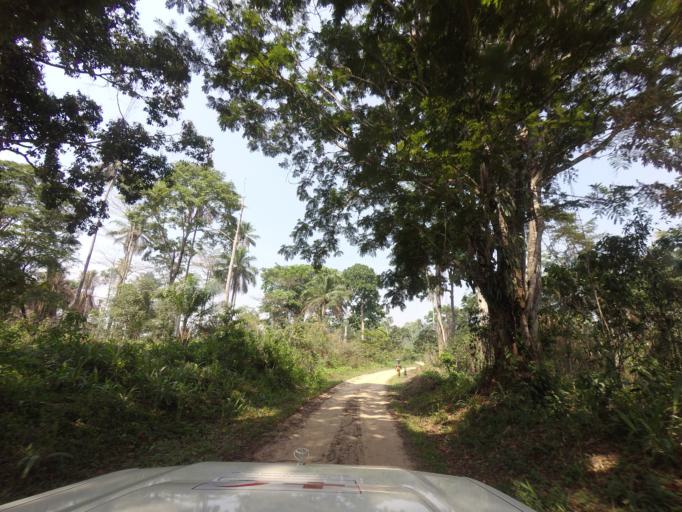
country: LR
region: Lofa
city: Voinjama
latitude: 8.5037
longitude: -9.6382
